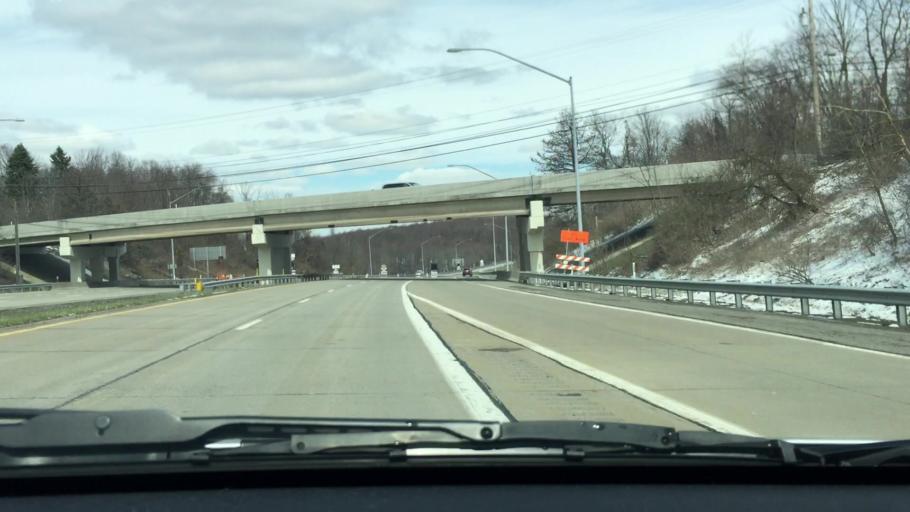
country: US
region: Pennsylvania
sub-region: Allegheny County
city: Carnot-Moon
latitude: 40.5162
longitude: -80.2716
